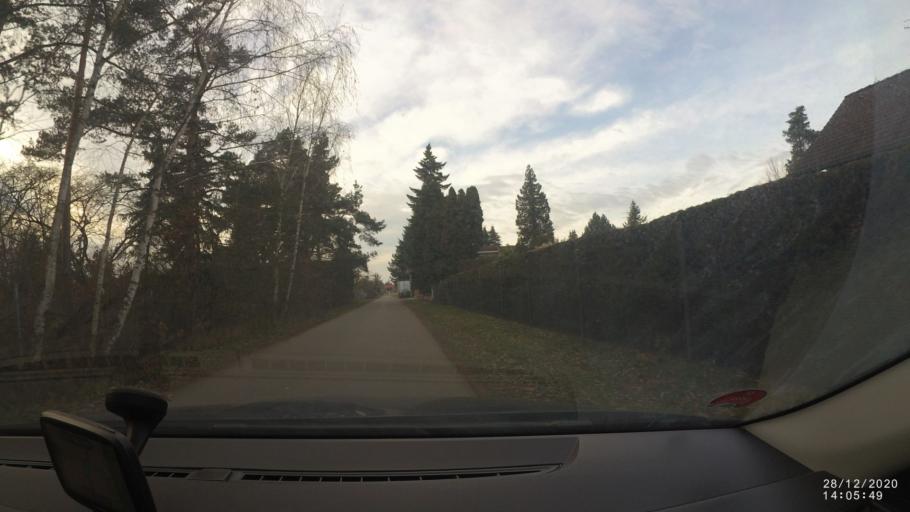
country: CZ
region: Central Bohemia
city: Sestajovice
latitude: 50.1003
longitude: 14.6661
